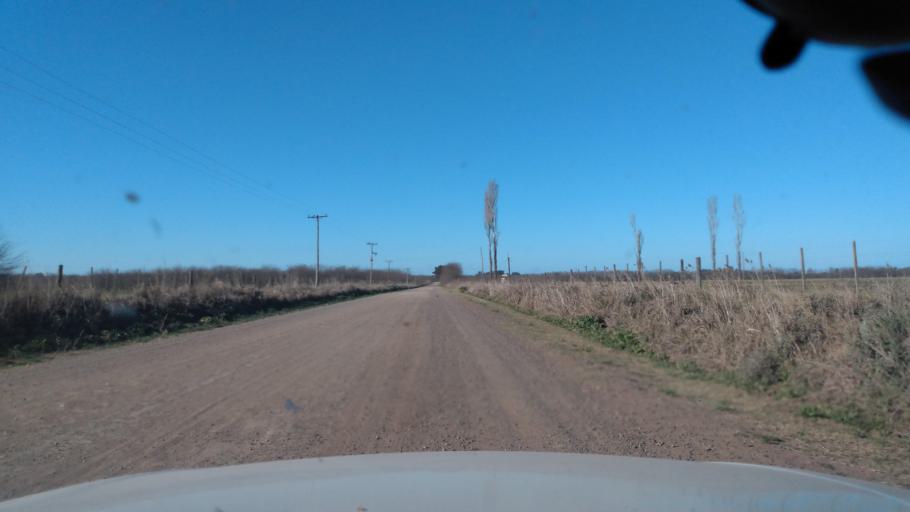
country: AR
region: Buenos Aires
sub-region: Partido de Mercedes
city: Mercedes
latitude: -34.6166
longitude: -59.3346
